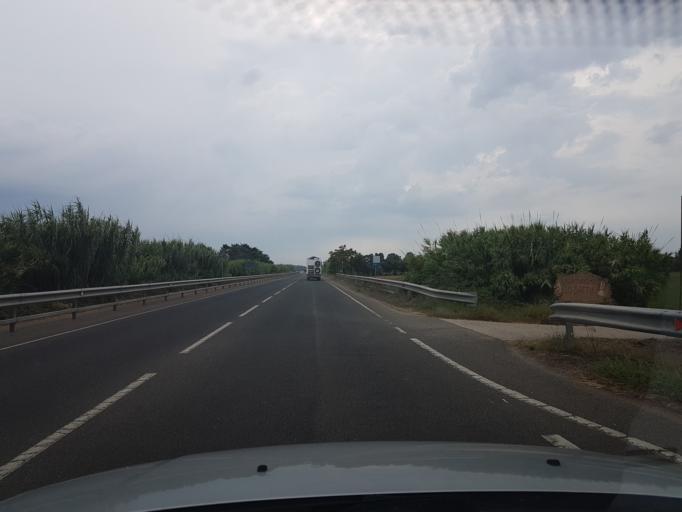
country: IT
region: Sardinia
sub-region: Provincia di Oristano
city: Solanas
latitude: 39.9159
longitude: 8.5477
